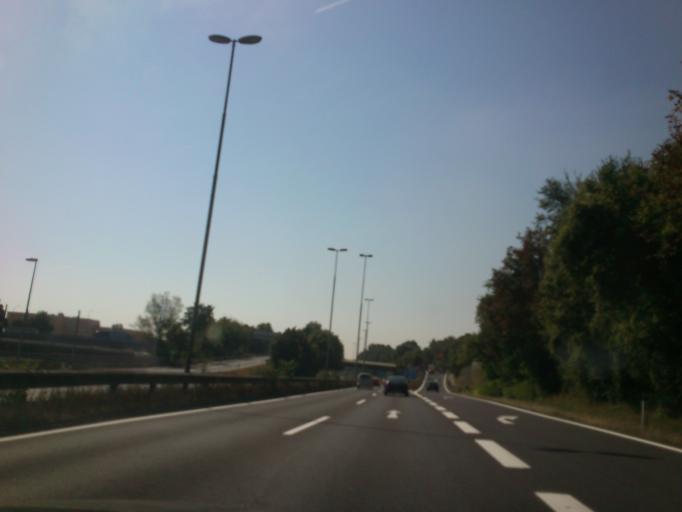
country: AT
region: Upper Austria
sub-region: Linz Stadt
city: Linz
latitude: 48.3035
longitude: 14.3139
